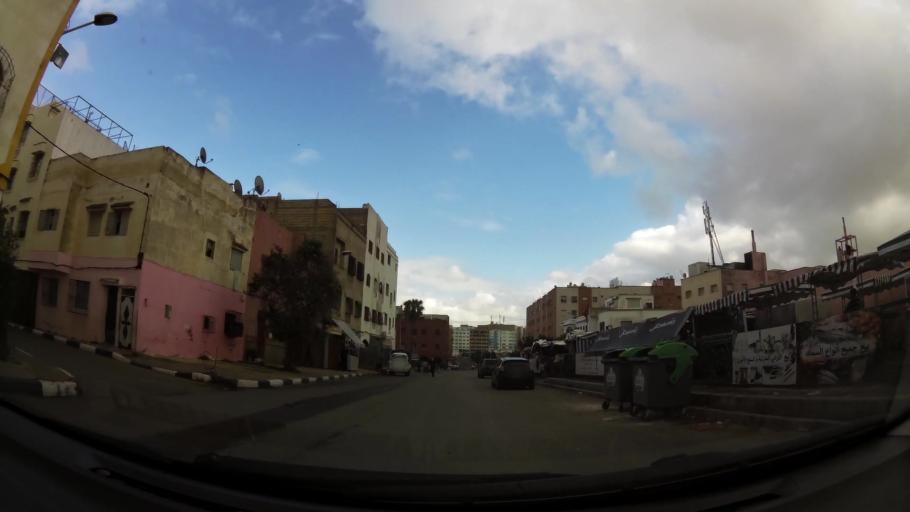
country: MA
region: Grand Casablanca
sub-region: Casablanca
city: Casablanca
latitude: 33.5594
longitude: -7.6938
